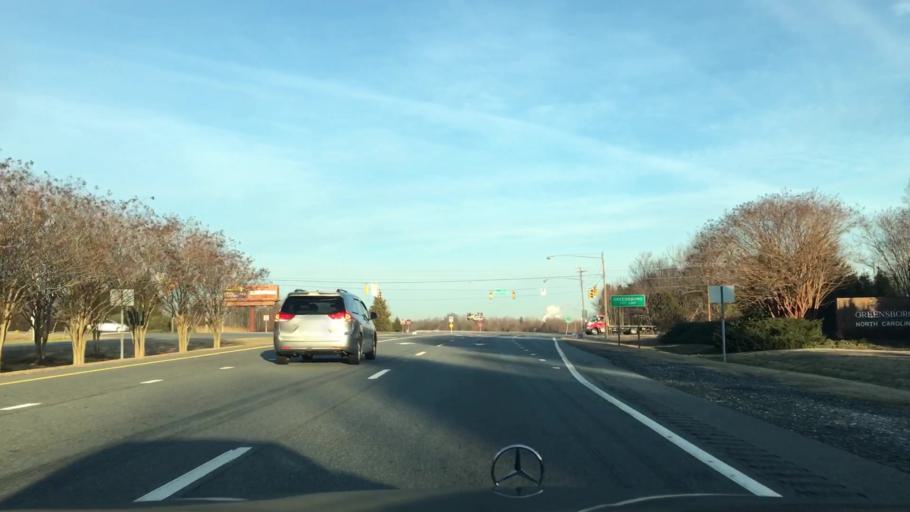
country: US
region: North Carolina
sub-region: Guilford County
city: Greensboro
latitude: 36.0272
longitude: -79.7693
